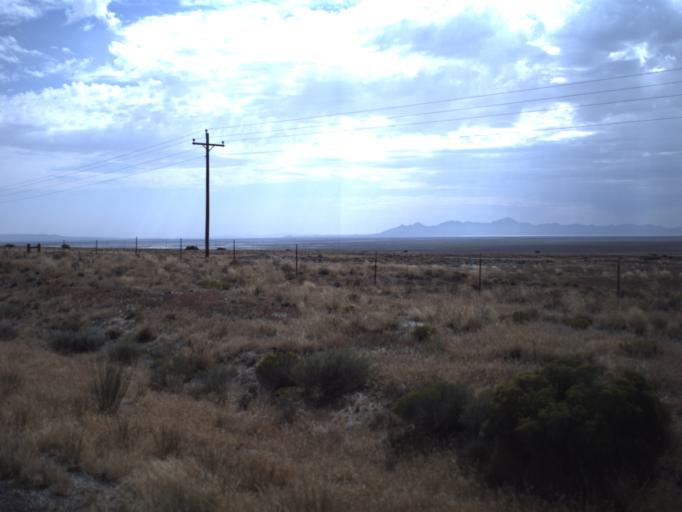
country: US
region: Utah
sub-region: Tooele County
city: Wendover
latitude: 41.4345
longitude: -113.7650
